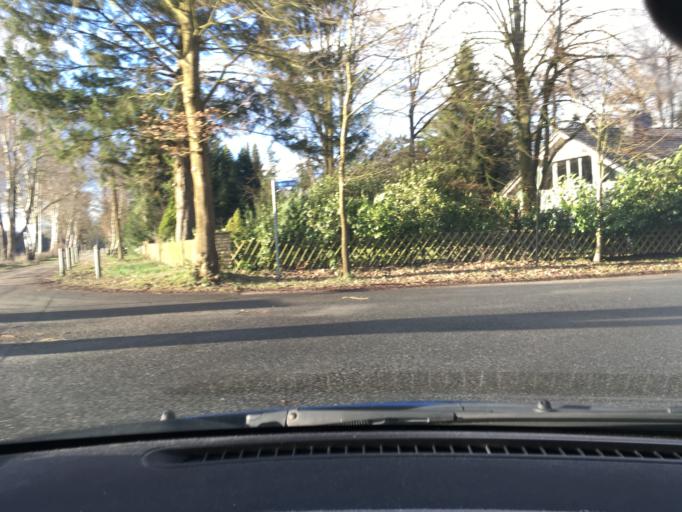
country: DE
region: Lower Saxony
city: Jesteburg
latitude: 53.3085
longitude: 9.9845
